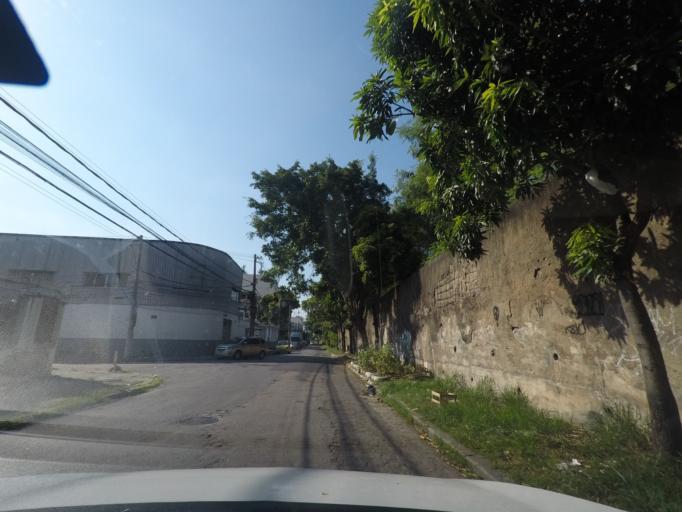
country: BR
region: Rio de Janeiro
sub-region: Rio De Janeiro
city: Rio de Janeiro
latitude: -22.8600
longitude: -43.2576
